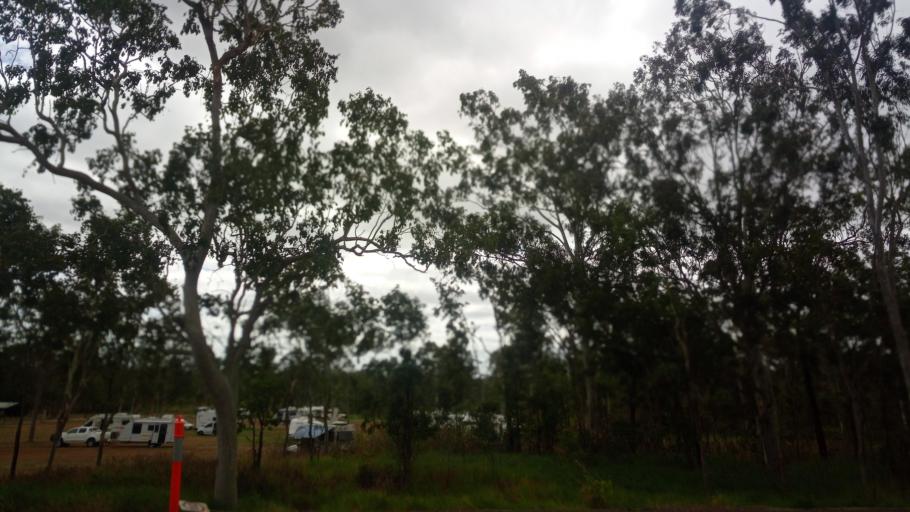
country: AU
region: Queensland
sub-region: Tablelands
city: Tolga
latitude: -17.1828
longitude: 145.4563
